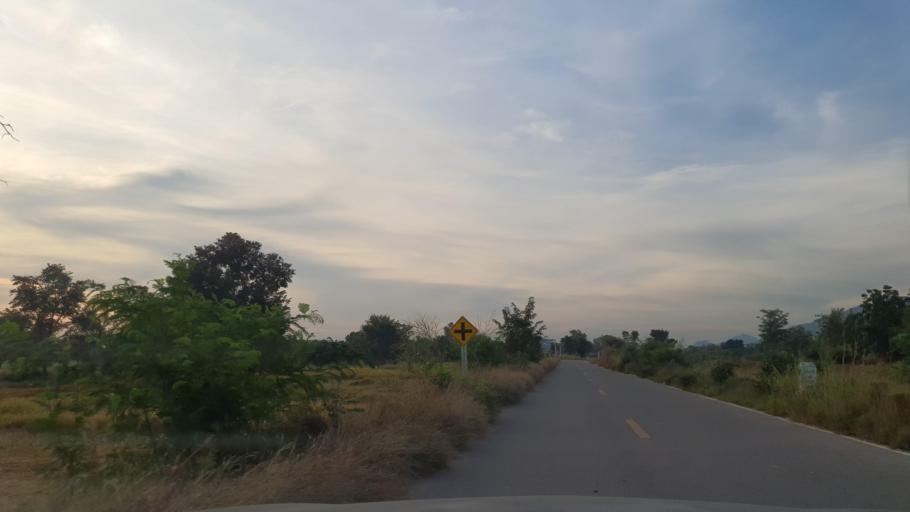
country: TH
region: Uthai Thani
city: Sawang Arom
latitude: 15.7121
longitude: 99.9570
